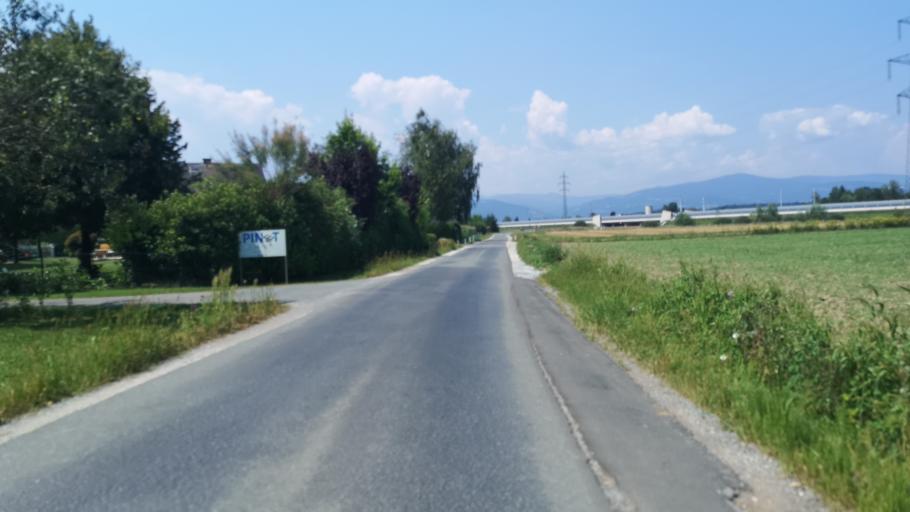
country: AT
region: Styria
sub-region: Politischer Bezirk Deutschlandsberg
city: Gross Sankt Florian
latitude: 46.8143
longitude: 15.3286
